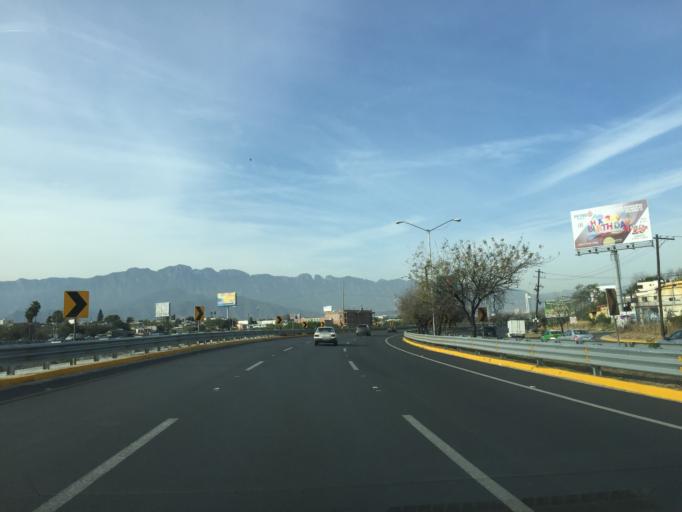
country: MX
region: Nuevo Leon
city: Guadalupe
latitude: 25.6860
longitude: -100.2498
